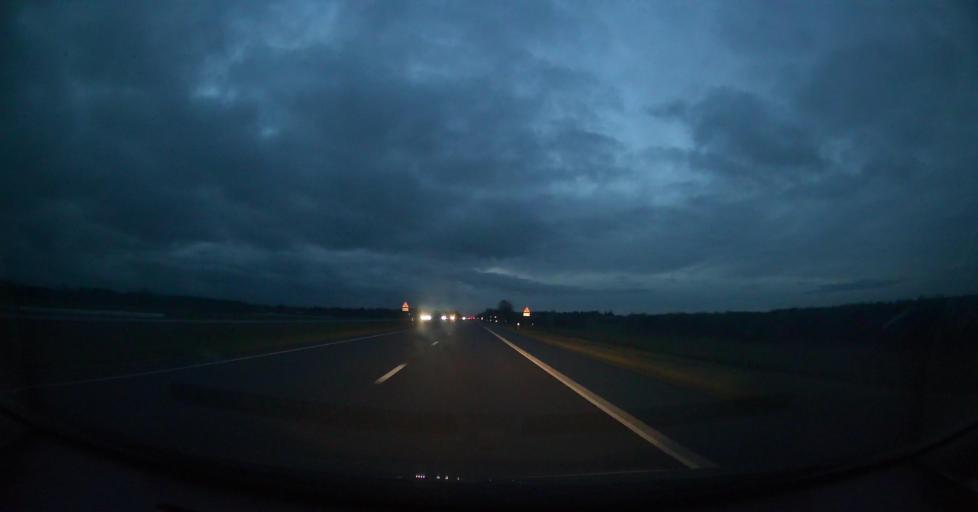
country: EE
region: Harju
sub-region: Anija vald
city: Kehra
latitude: 59.4423
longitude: 25.3170
